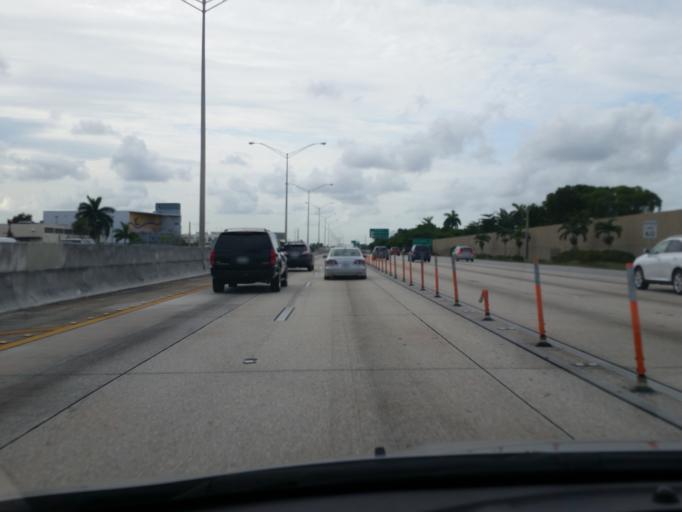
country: US
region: Florida
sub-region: Miami-Dade County
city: El Portal
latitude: 25.8519
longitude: -80.2079
